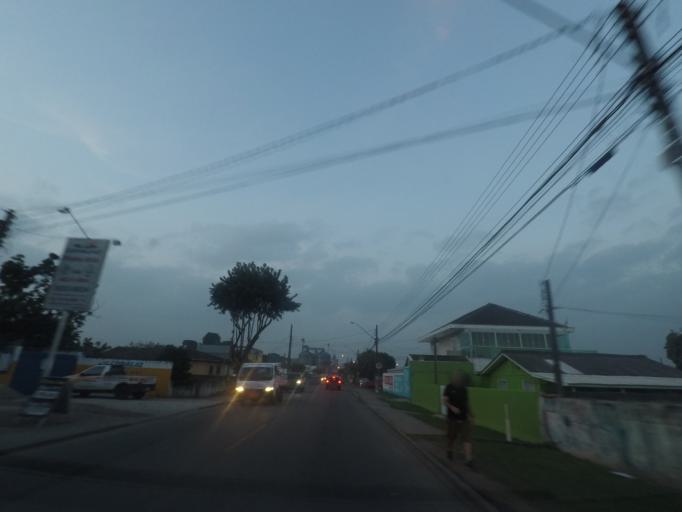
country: BR
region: Parana
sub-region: Pinhais
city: Pinhais
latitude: -25.4501
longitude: -49.1893
